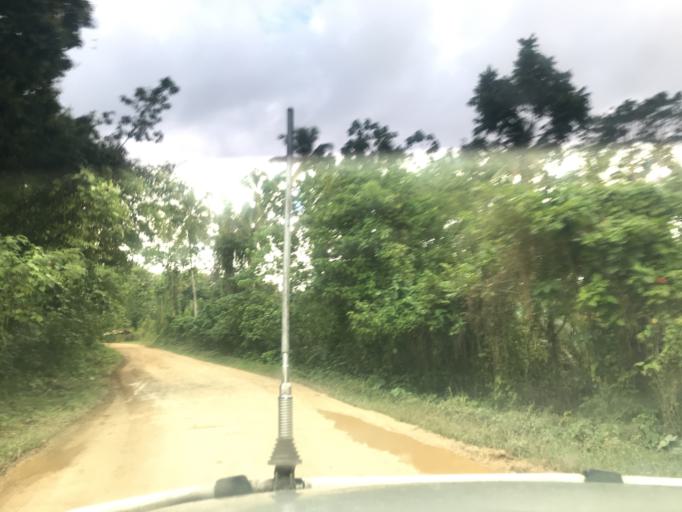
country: SB
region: Malaita
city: Auki
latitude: -8.6555
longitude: 160.6707
